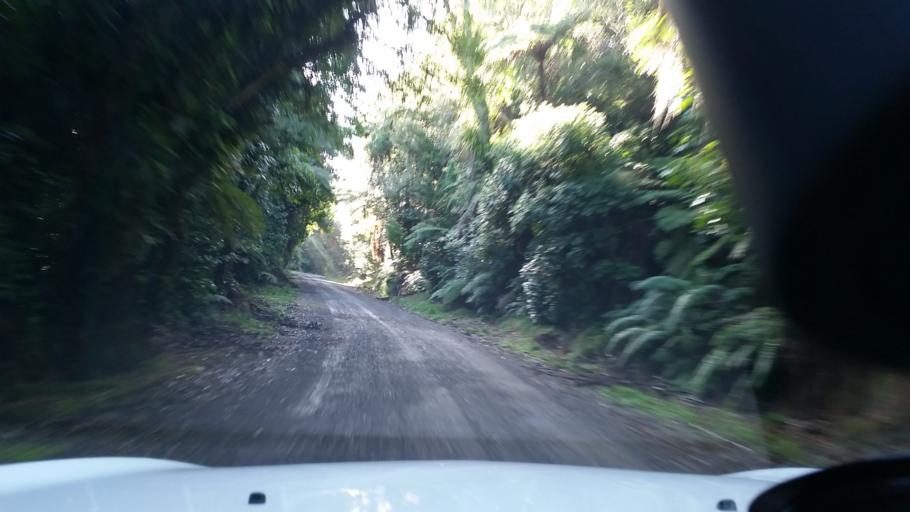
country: NZ
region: Bay of Plenty
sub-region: Kawerau District
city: Kawerau
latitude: -38.0206
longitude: 176.5763
